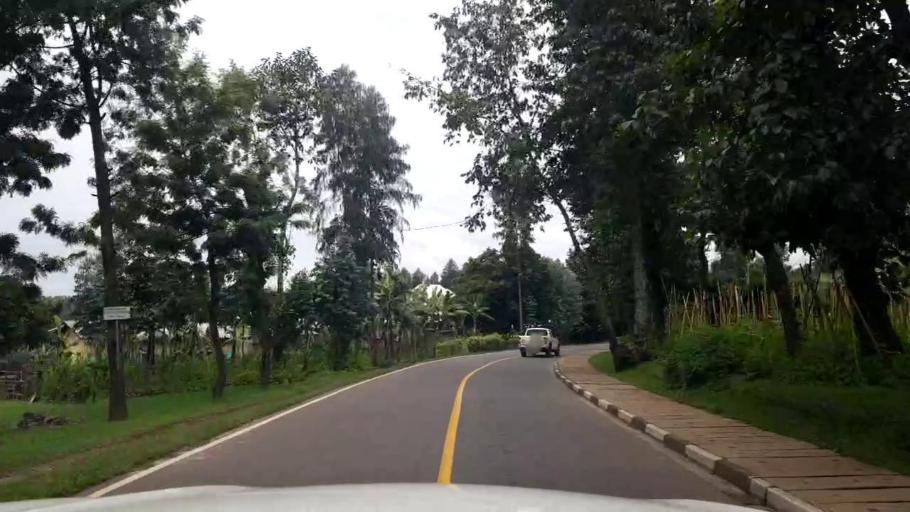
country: RW
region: Northern Province
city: Musanze
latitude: -1.4554
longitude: 29.6091
